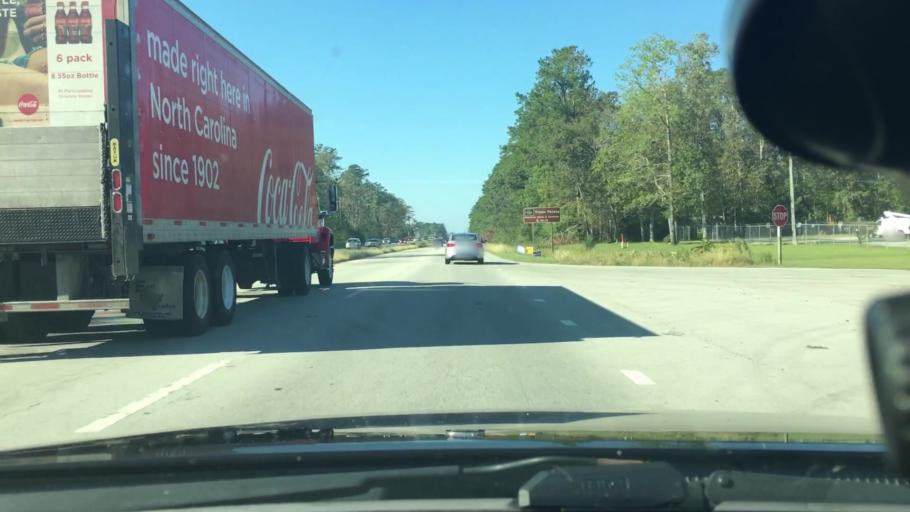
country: US
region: North Carolina
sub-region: Craven County
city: James City
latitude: 35.0406
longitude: -77.0086
